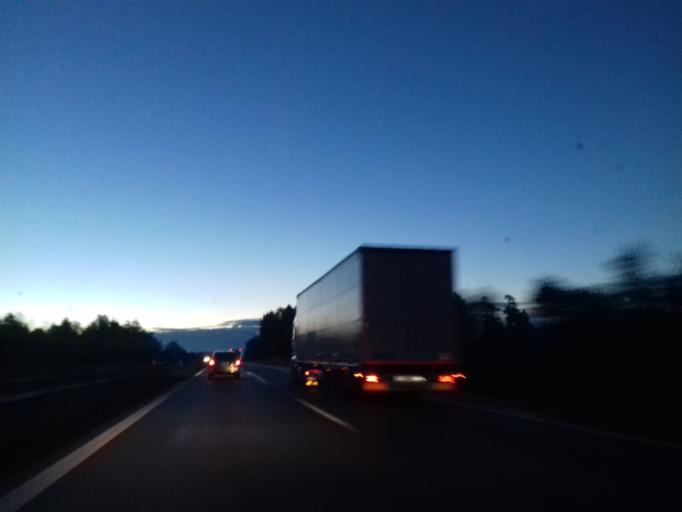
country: CZ
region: Vysocina
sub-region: Okres Zd'ar nad Sazavou
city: Velke Mezirici
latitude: 49.3334
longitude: 16.0661
